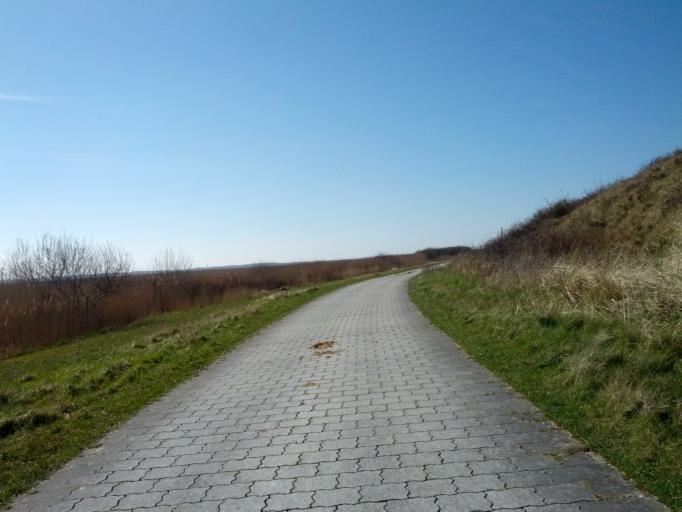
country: DE
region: Lower Saxony
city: Langeoog
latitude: 53.7507
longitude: 7.5788
